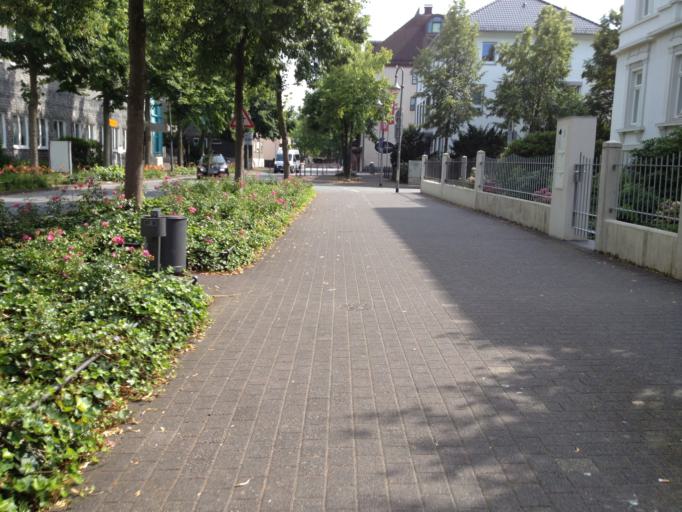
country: DE
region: North Rhine-Westphalia
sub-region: Regierungsbezirk Detmold
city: Guetersloh
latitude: 51.9072
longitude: 8.3823
